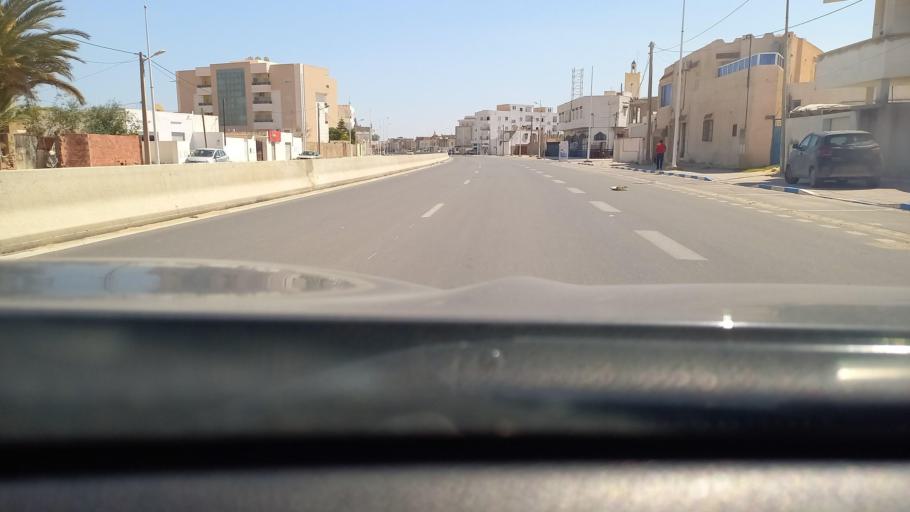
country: TN
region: Safaqis
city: Sfax
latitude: 34.7418
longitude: 10.7241
